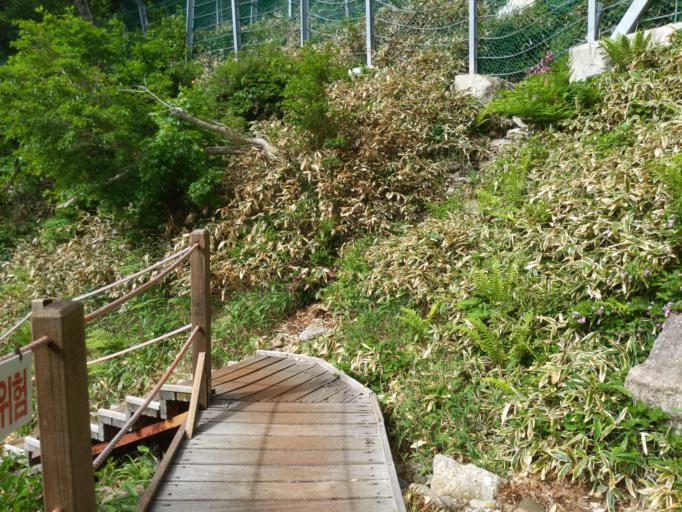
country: KR
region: Jeju-do
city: Seogwipo
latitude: 33.3742
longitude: 126.5297
